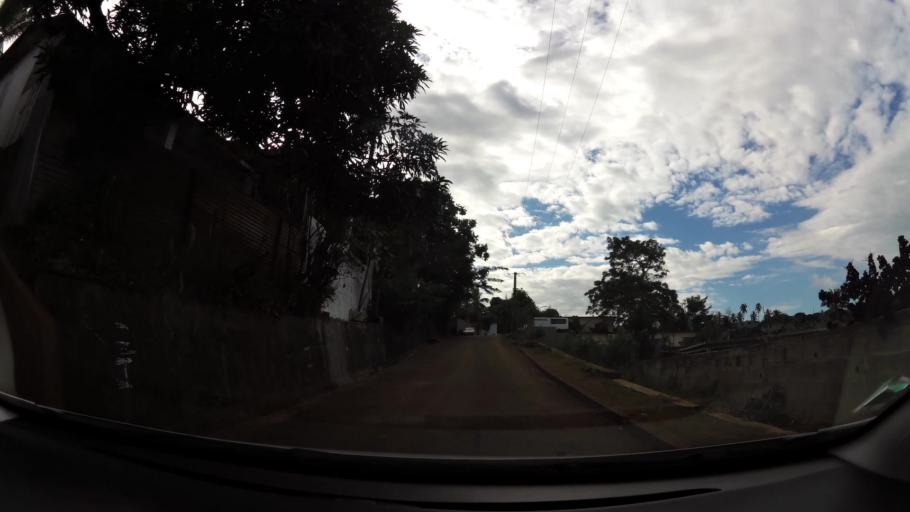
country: YT
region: Ouangani
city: Ouangani
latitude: -12.8385
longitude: 45.1323
